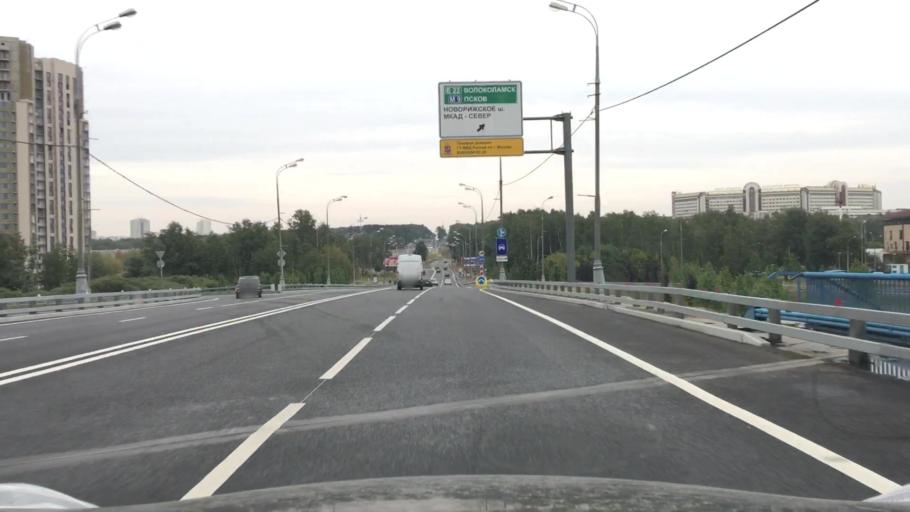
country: RU
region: Moscow
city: Rublevo
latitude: 55.7695
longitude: 37.3702
